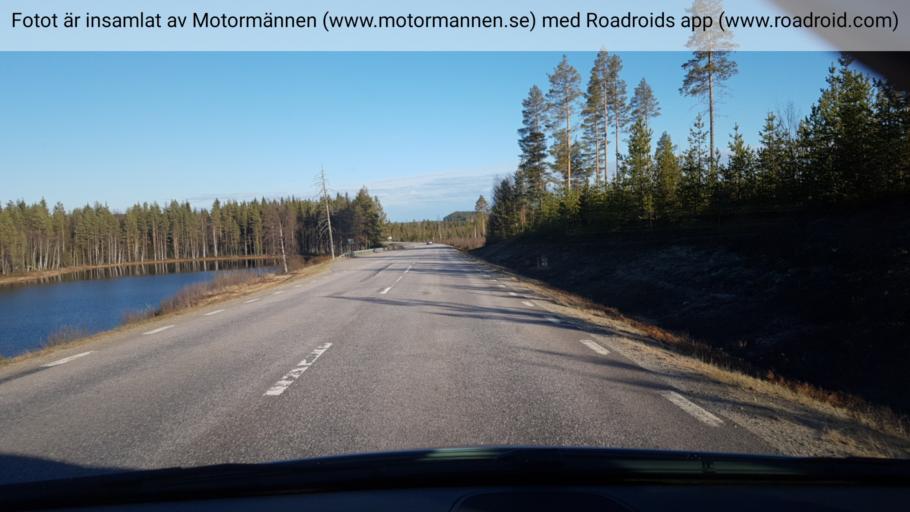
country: SE
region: Vaesterbotten
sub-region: Vindelns Kommun
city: Vindeln
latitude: 64.0581
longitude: 19.6474
